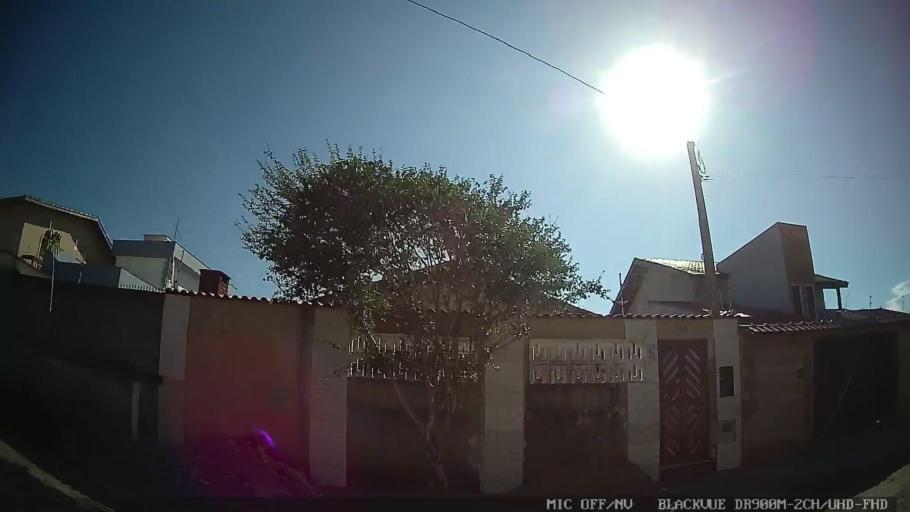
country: BR
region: Sao Paulo
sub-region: Peruibe
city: Peruibe
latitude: -24.2783
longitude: -46.9447
